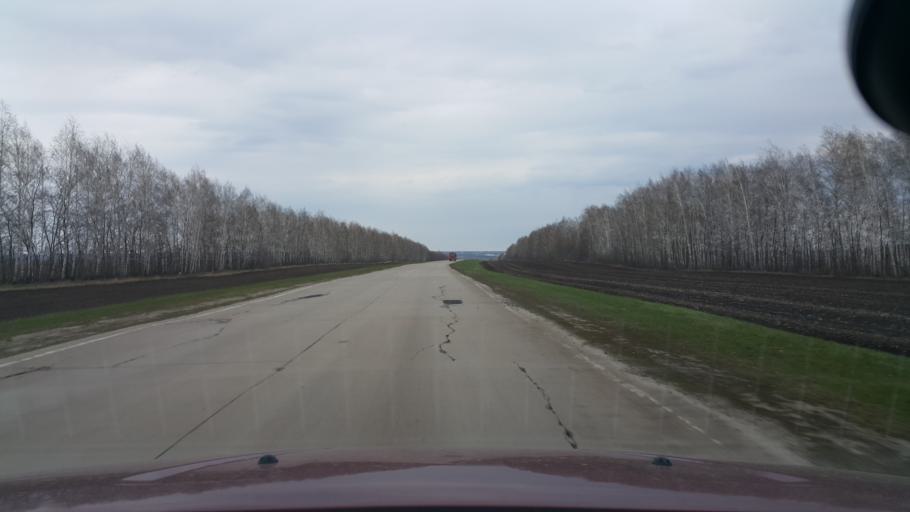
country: RU
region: Tambov
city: Bokino
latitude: 52.5710
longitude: 41.3991
